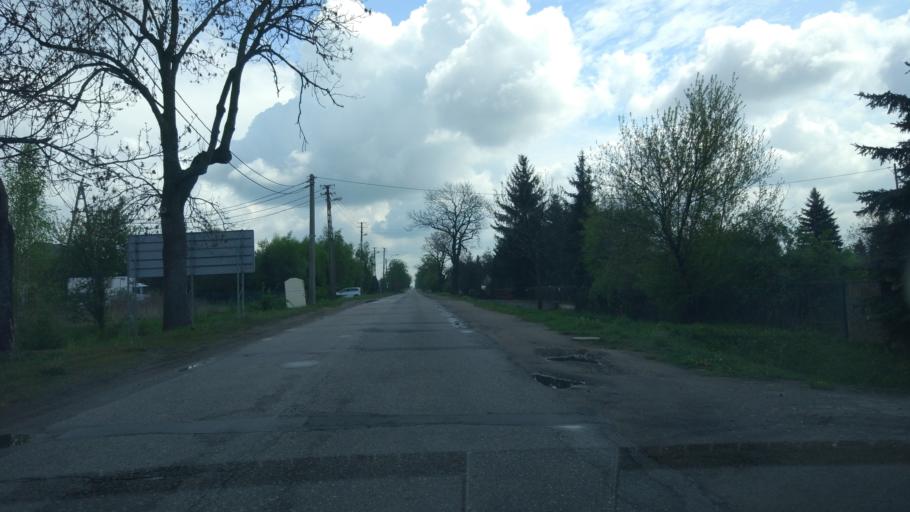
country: PL
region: Lodz Voivodeship
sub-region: Powiat kutnowski
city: Kutno
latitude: 52.2272
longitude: 19.3887
